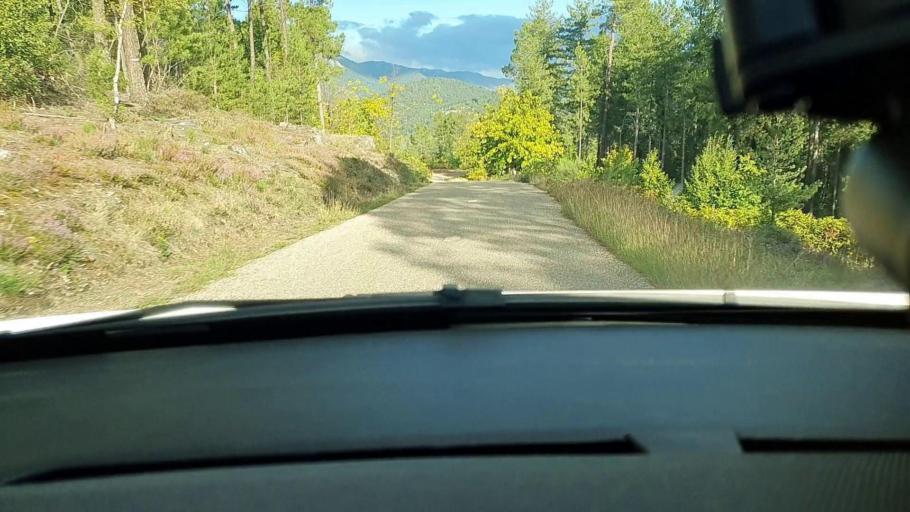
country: FR
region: Languedoc-Roussillon
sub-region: Departement du Gard
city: Besseges
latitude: 44.3440
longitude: 3.9858
